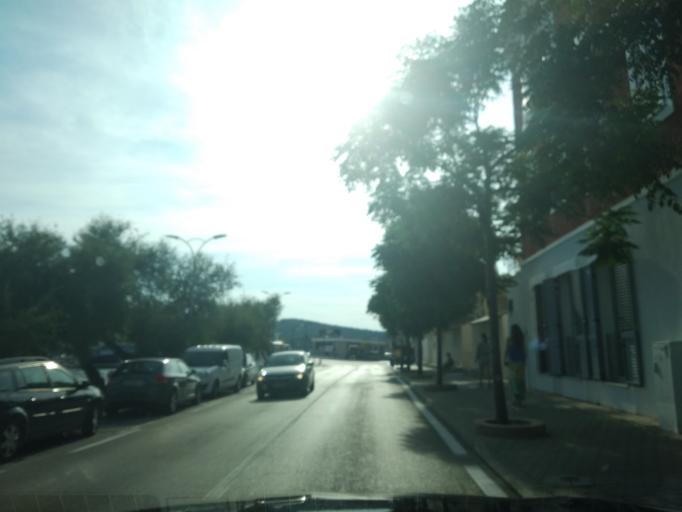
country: HR
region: Sibensko-Kniniska
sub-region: Grad Sibenik
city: Tisno
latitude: 43.7994
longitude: 15.6429
